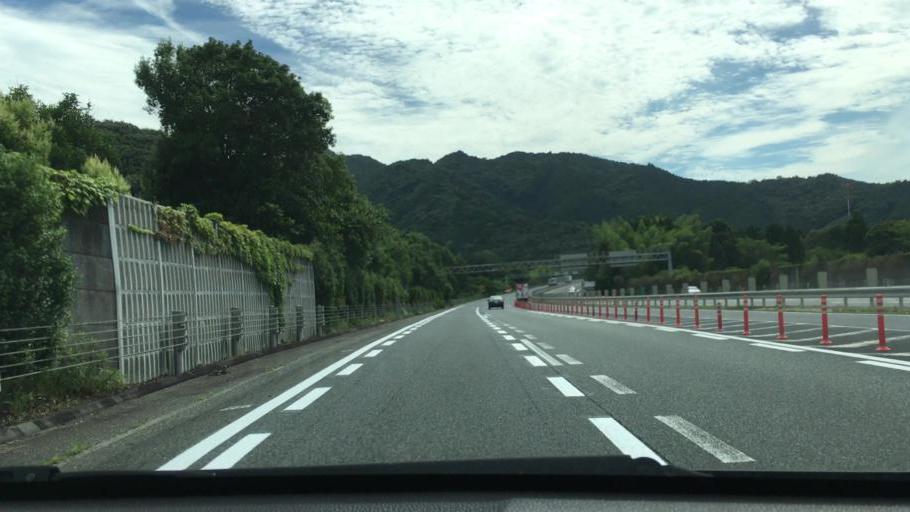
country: JP
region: Yamaguchi
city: Ogori-shimogo
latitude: 34.1310
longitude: 131.4452
